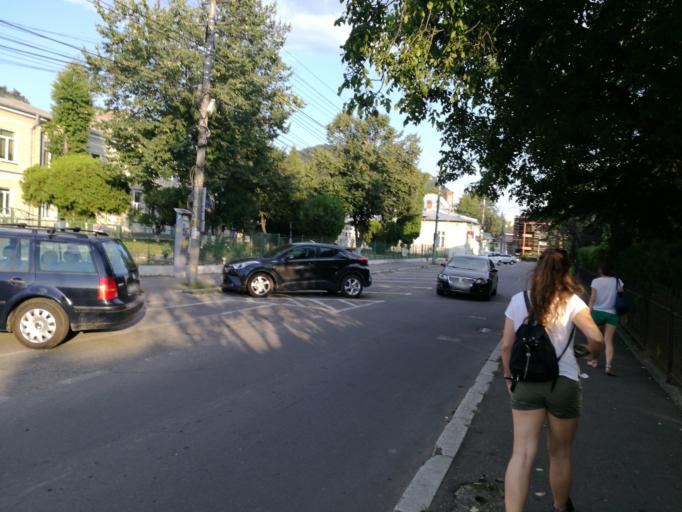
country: RO
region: Neamt
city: Piatra Neamt
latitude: 46.9341
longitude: 26.3635
